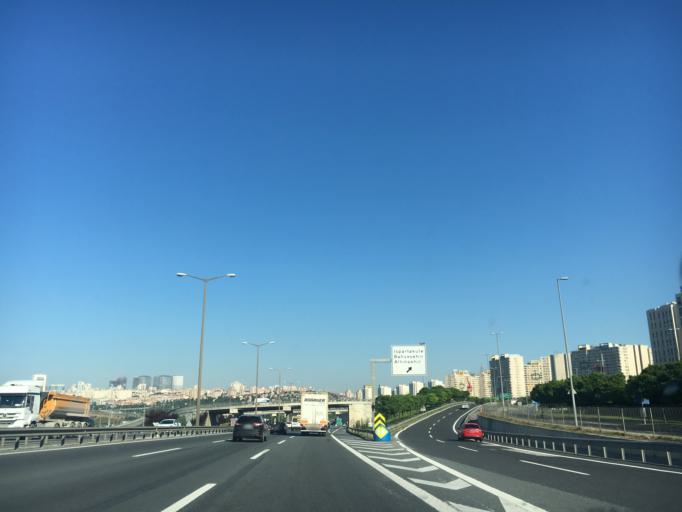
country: TR
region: Istanbul
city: Esenyurt
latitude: 41.0555
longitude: 28.7148
